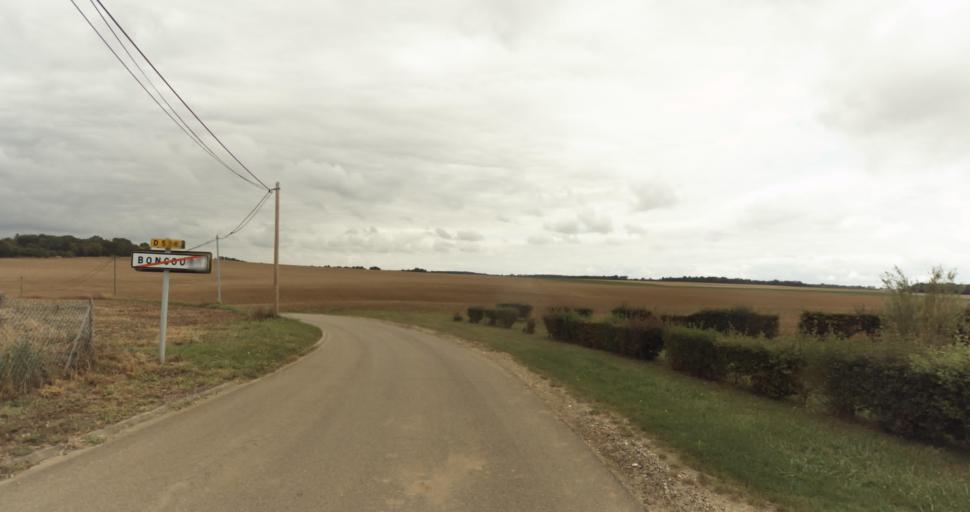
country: FR
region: Haute-Normandie
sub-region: Departement de l'Eure
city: Menilles
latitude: 49.0216
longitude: 1.3013
